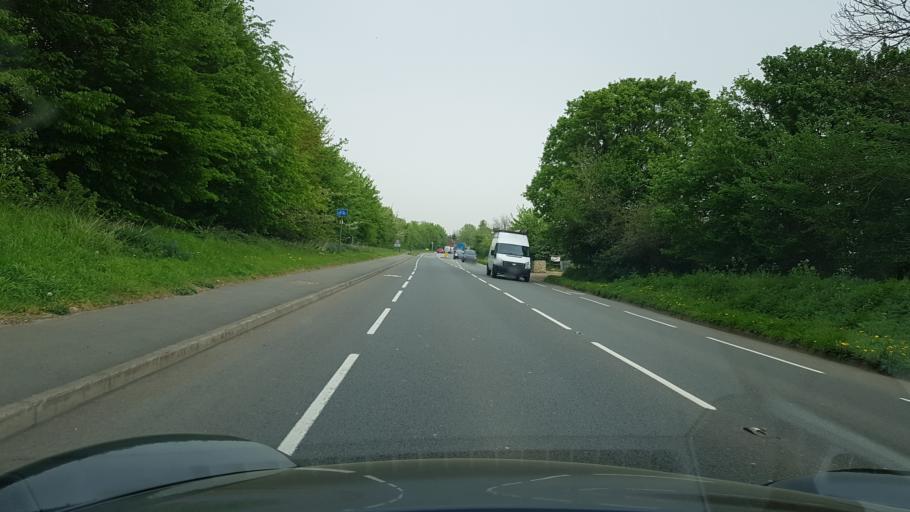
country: GB
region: England
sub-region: Surrey
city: Ripley
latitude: 51.2964
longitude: -0.4993
